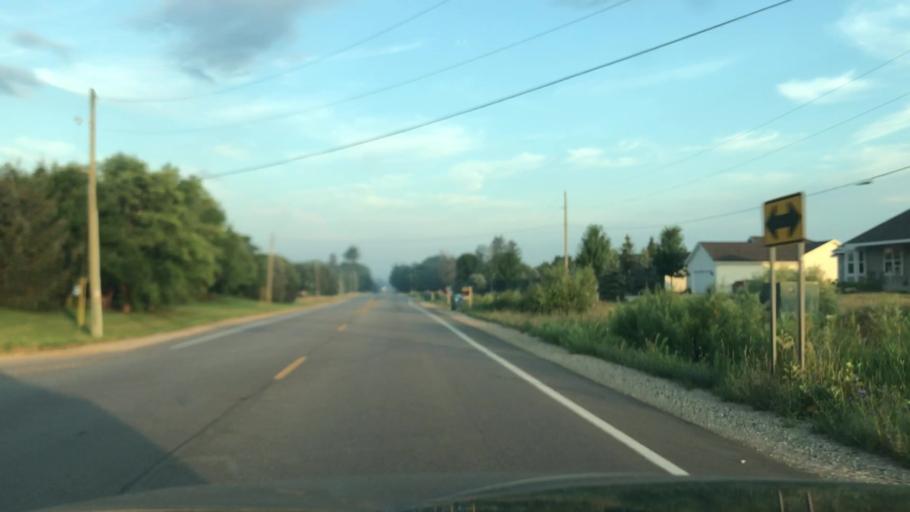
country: US
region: Michigan
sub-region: Ottawa County
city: Zeeland
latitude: 42.7833
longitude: -85.9703
